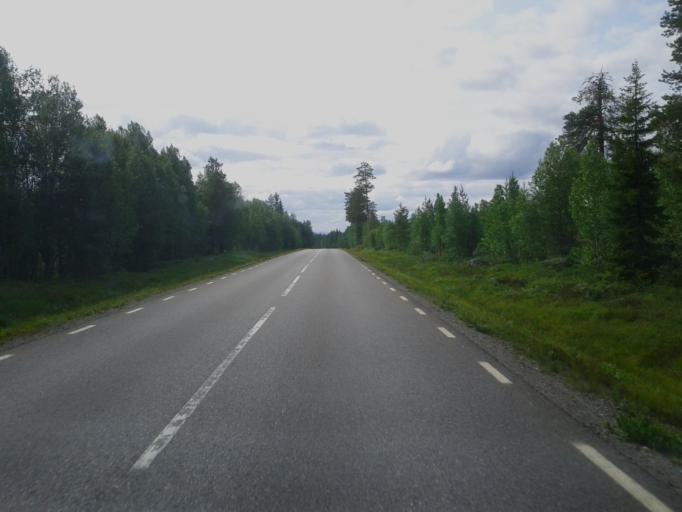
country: SE
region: Vaesterbotten
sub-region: Lycksele Kommun
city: Soderfors
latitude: 65.2561
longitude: 18.2407
